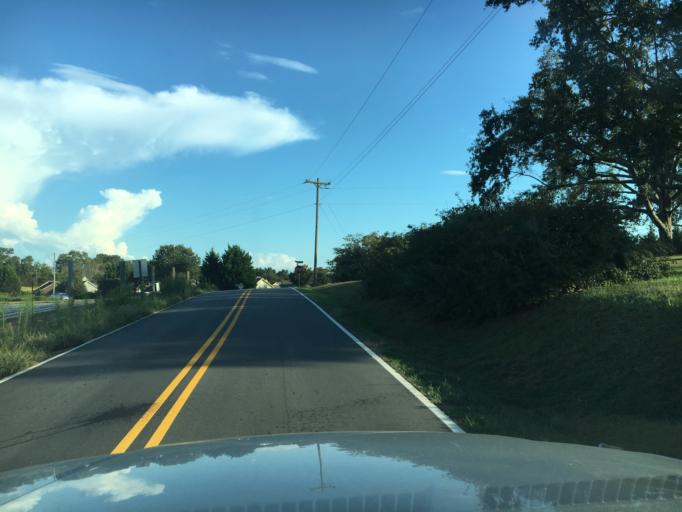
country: US
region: South Carolina
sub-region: Spartanburg County
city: Roebuck
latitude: 34.8813
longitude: -82.0196
